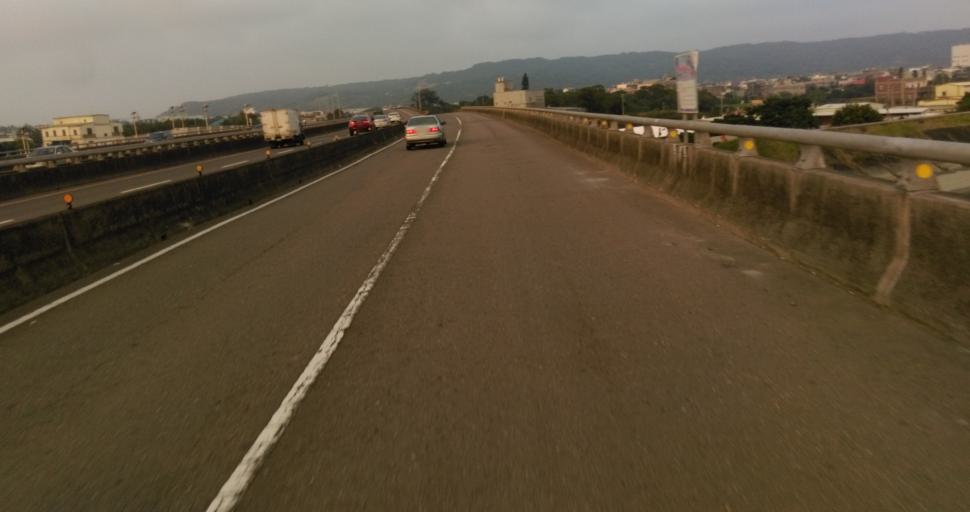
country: TW
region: Taiwan
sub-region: Hsinchu
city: Hsinchu
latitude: 24.8589
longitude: 120.9497
